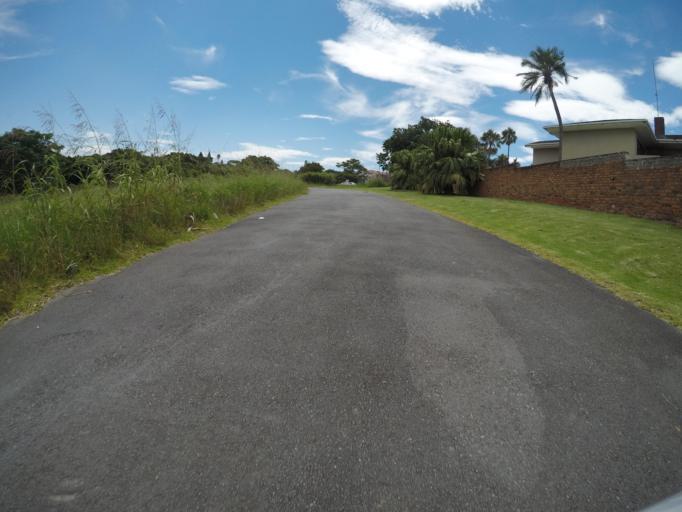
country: ZA
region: Eastern Cape
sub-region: Buffalo City Metropolitan Municipality
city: East London
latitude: -33.0423
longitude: 27.8536
